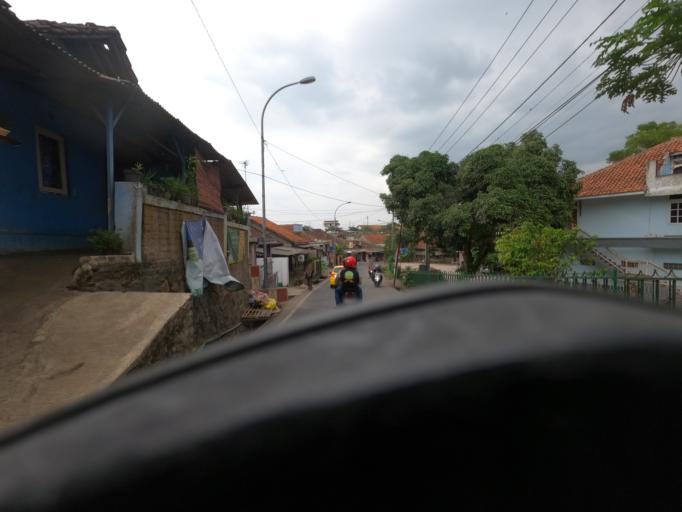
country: ID
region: West Java
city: Padalarang
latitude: -6.8435
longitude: 107.5002
